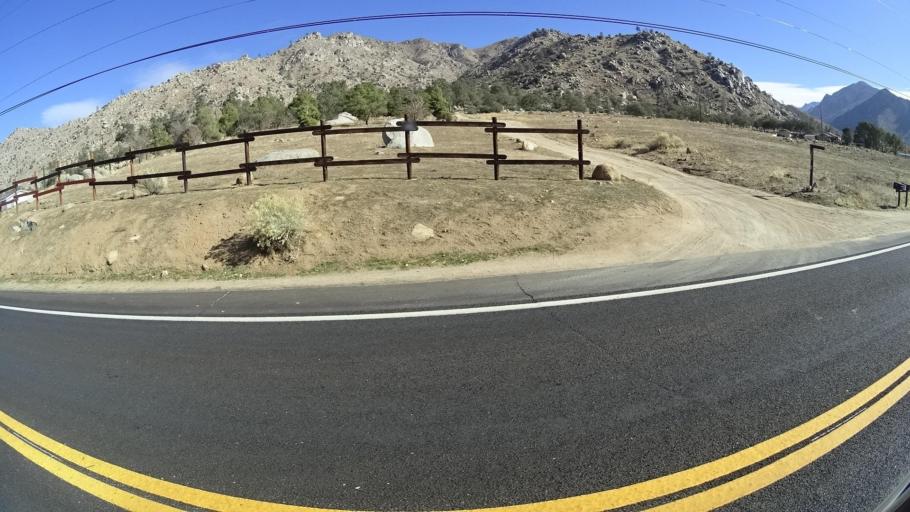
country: US
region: California
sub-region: Kern County
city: Lake Isabella
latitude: 35.6137
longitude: -118.4685
